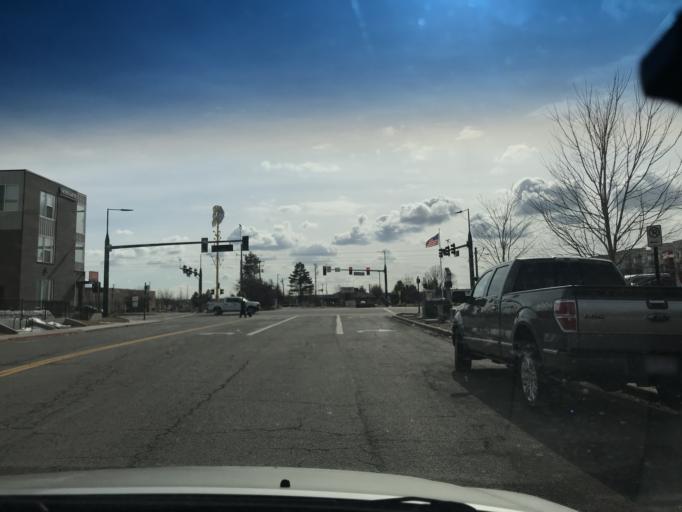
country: US
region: Utah
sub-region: Salt Lake County
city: Salt Lake City
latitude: 40.7723
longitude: -111.9471
